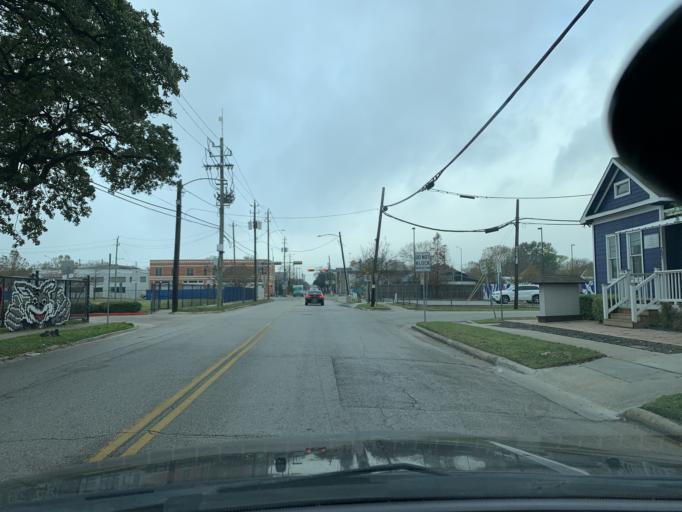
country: US
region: Texas
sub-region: Harris County
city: Houston
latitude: 29.7812
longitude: -95.3628
